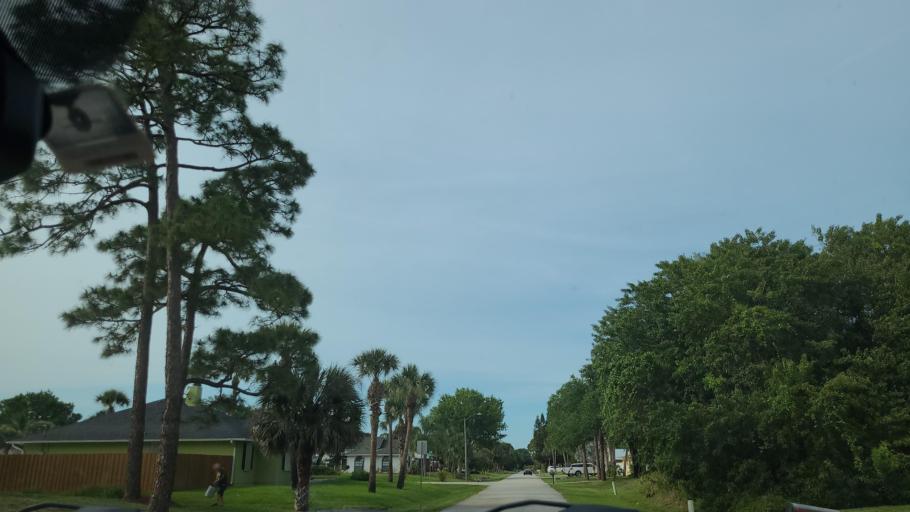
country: US
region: Florida
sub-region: Indian River County
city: Sebastian
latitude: 27.8073
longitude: -80.4789
